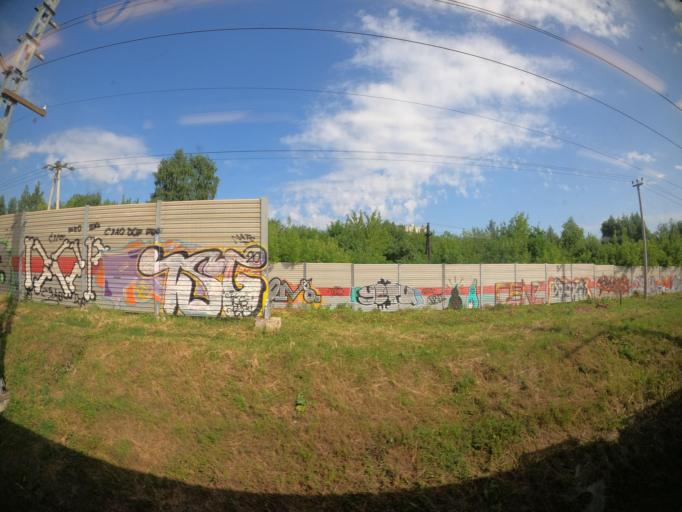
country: RU
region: Moscow
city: Tsaritsyno
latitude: 55.6134
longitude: 37.6489
